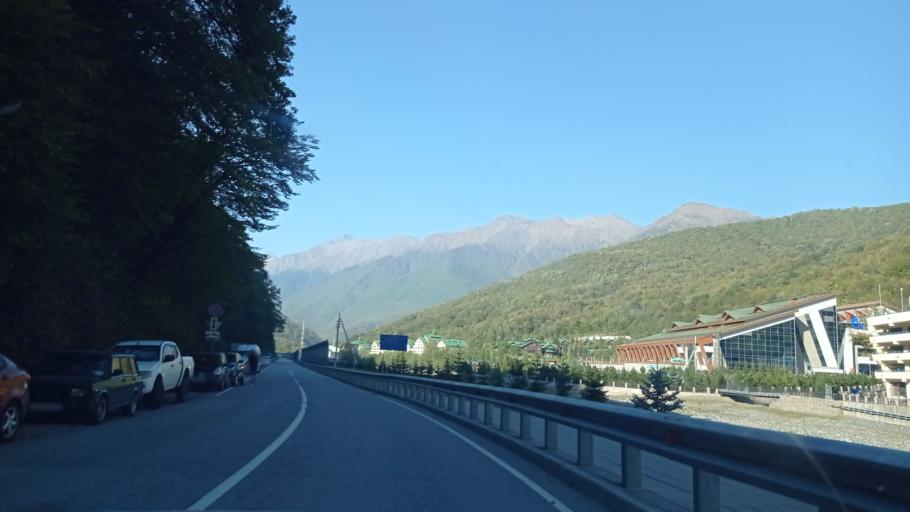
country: RU
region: Krasnodarskiy
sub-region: Sochi City
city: Krasnaya Polyana
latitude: 43.6832
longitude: 40.2784
